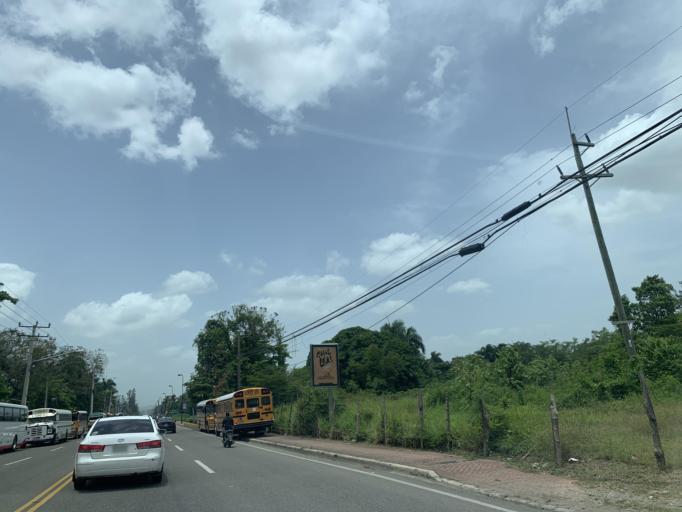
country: DO
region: Puerto Plata
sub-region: Puerto Plata
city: Puerto Plata
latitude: 19.7709
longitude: -70.6538
